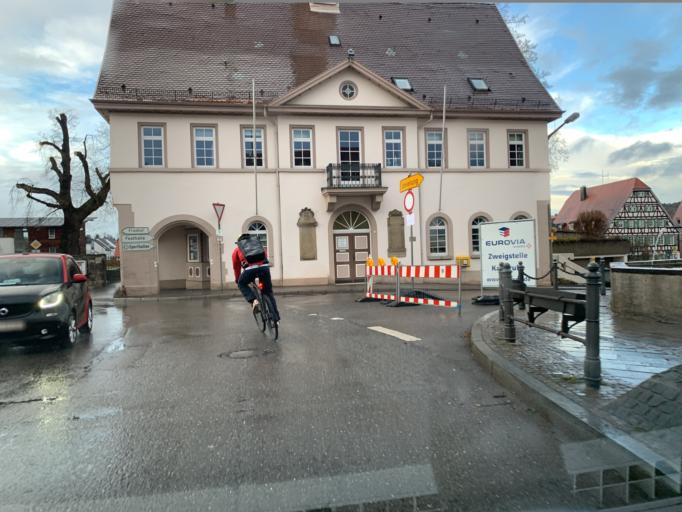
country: DE
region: Baden-Wuerttemberg
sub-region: Regierungsbezirk Stuttgart
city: Magstadt
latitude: 48.7418
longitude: 8.9630
